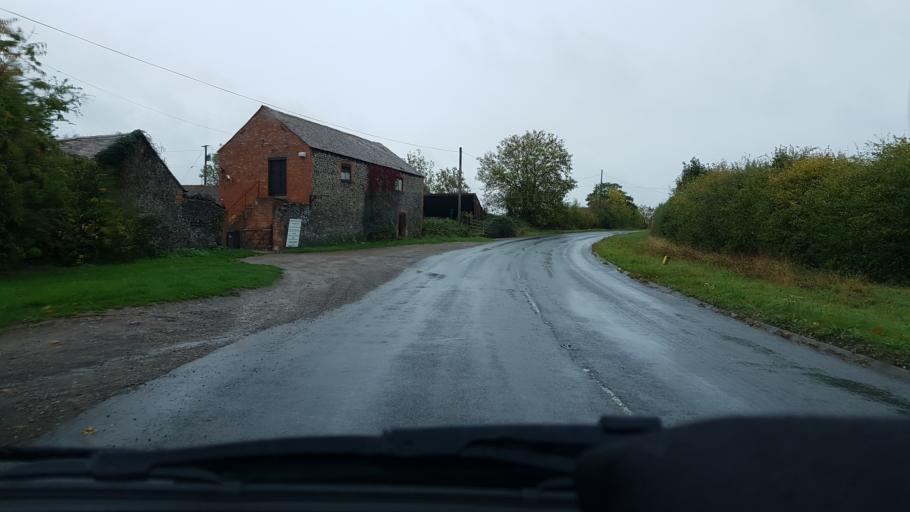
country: GB
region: England
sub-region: Worcestershire
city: Great Malvern
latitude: 52.0689
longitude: -2.2983
